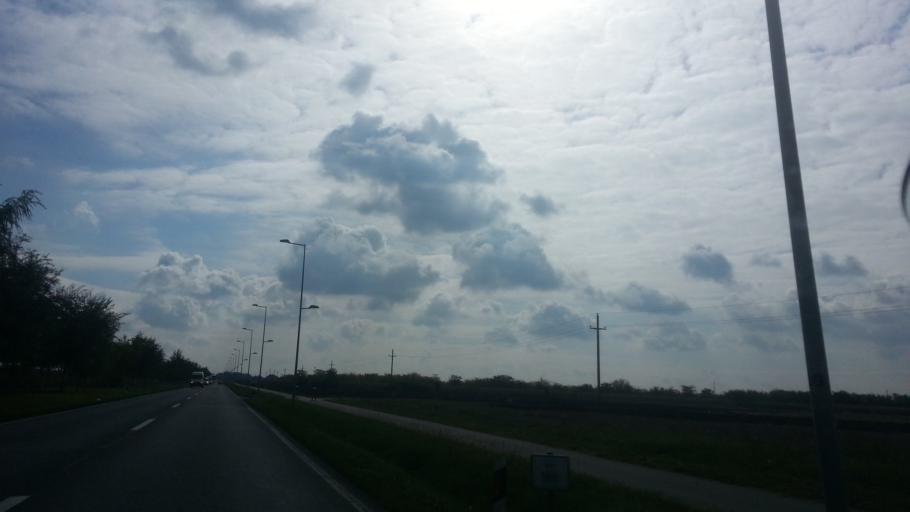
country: RS
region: Autonomna Pokrajina Vojvodina
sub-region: Sremski Okrug
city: Stara Pazova
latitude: 44.9644
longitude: 20.1878
